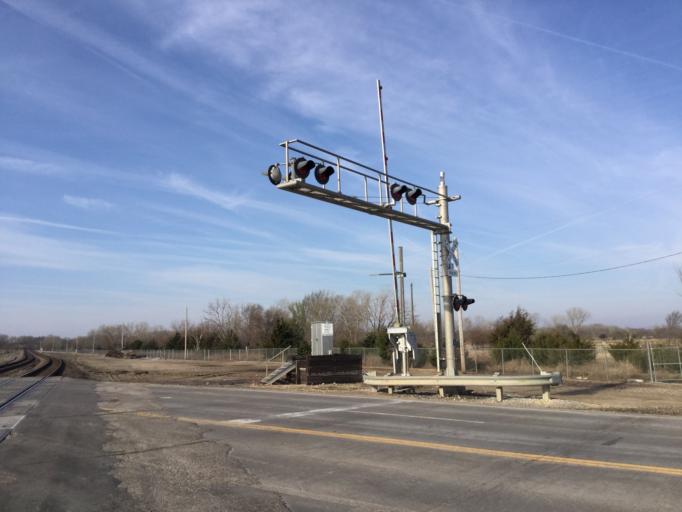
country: US
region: Kansas
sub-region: Butler County
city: Augusta
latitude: 37.6704
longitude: -96.9810
